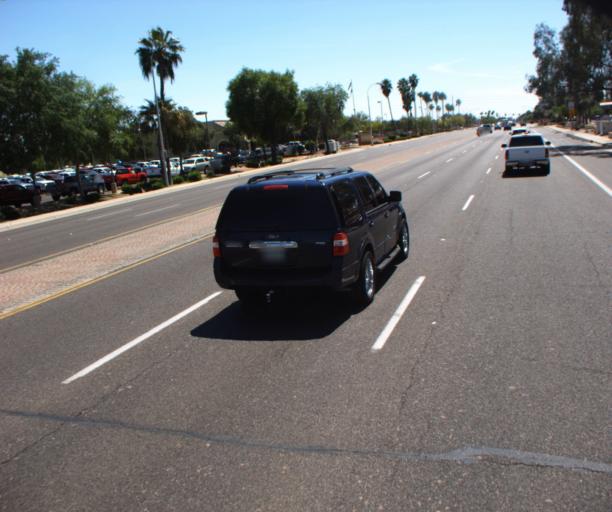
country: US
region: Arizona
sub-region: Maricopa County
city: San Carlos
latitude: 33.3386
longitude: -111.8419
